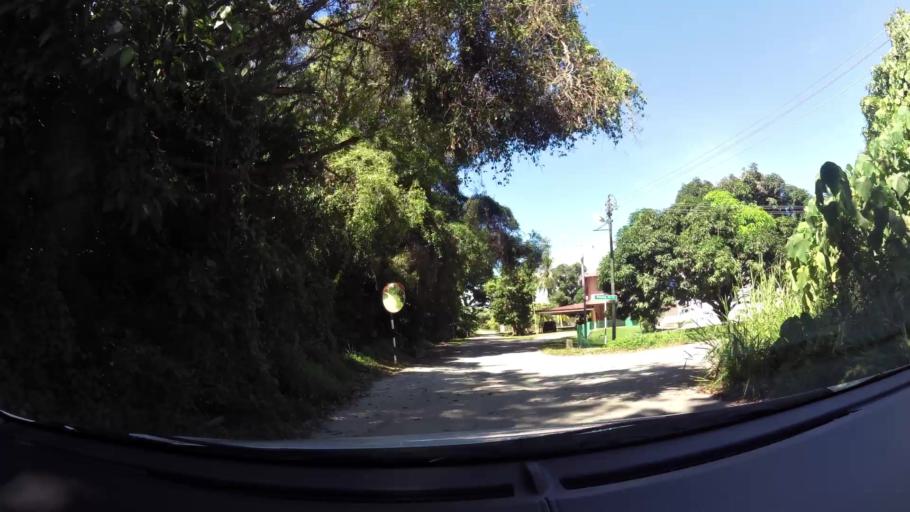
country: BN
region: Brunei and Muara
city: Bandar Seri Begawan
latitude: 5.0255
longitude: 115.0635
